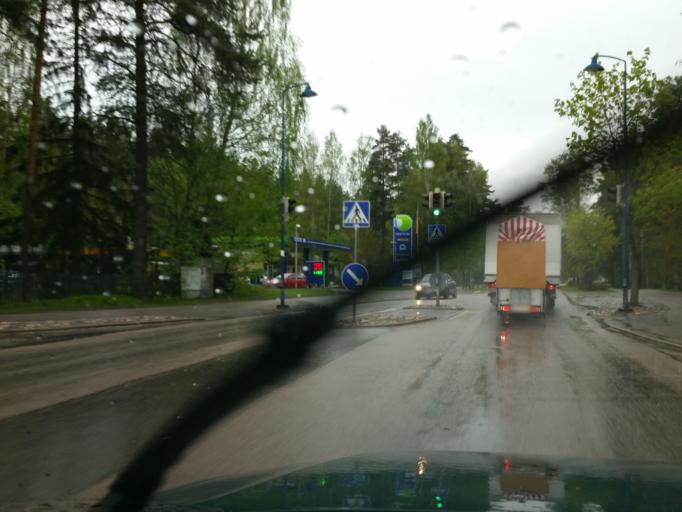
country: FI
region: Uusimaa
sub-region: Helsinki
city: Vihti
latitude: 60.3374
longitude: 24.3210
